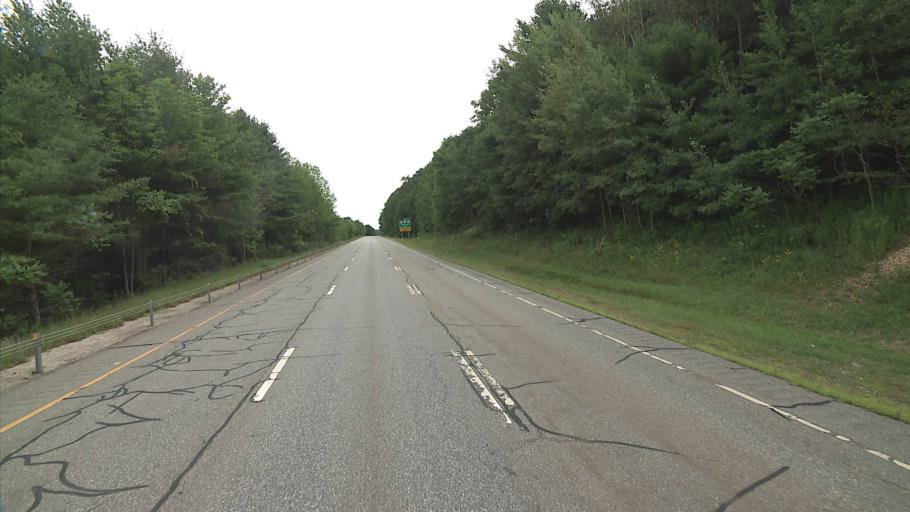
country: US
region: Connecticut
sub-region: Litchfield County
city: Winsted
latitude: 41.8984
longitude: -73.0671
